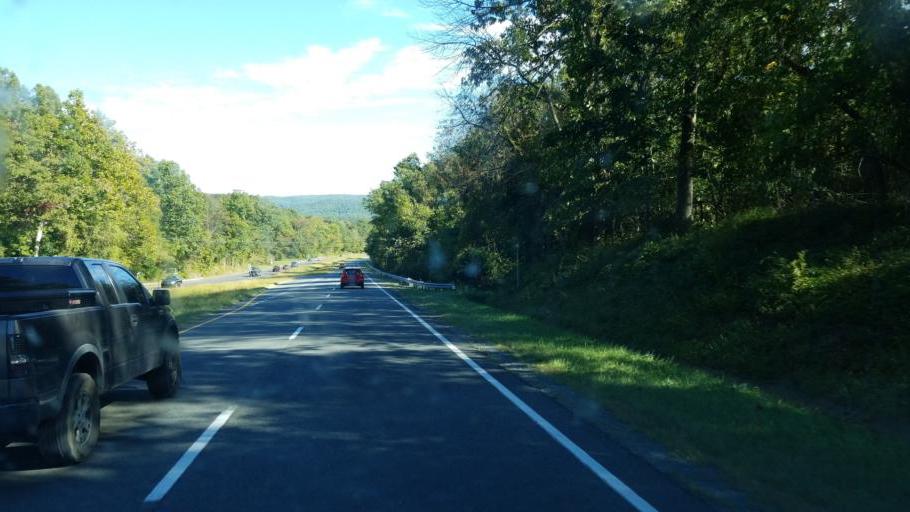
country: US
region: Virginia
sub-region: Warren County
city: Shenandoah Farms
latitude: 39.0473
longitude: -78.0097
